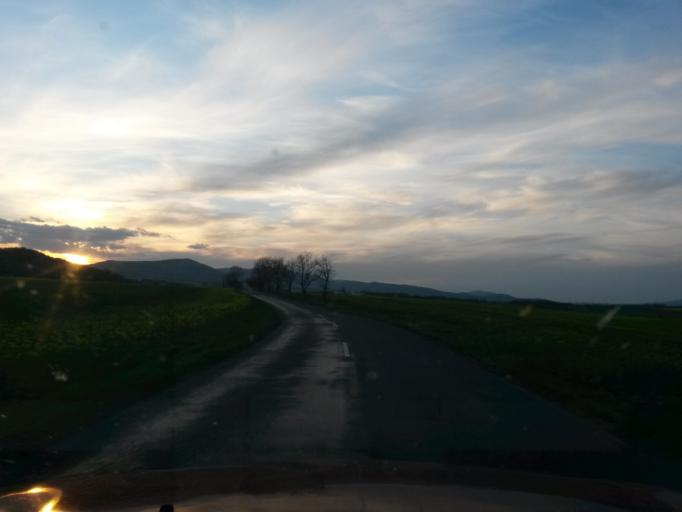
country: HU
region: Borsod-Abauj-Zemplen
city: Satoraljaujhely
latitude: 48.5134
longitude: 21.6071
